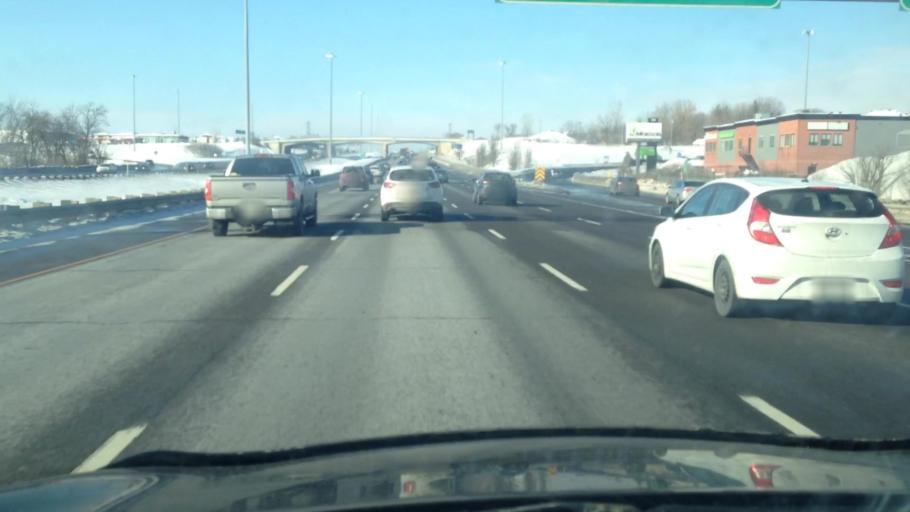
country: CA
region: Quebec
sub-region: Laurentides
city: Blainville
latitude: 45.6426
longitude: -73.8623
